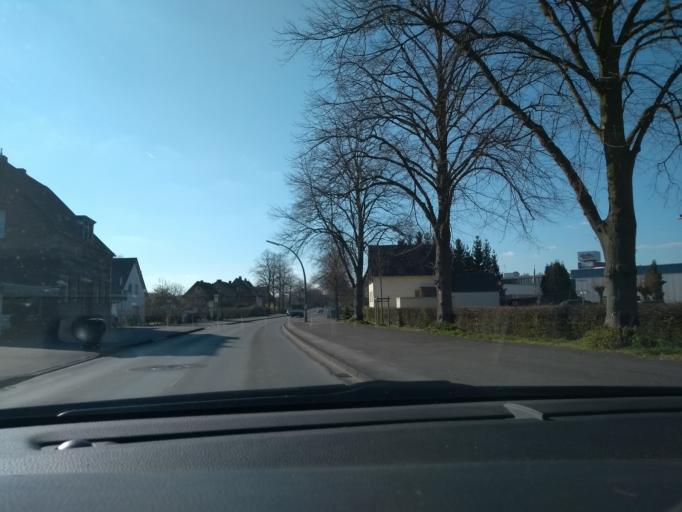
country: DE
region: North Rhine-Westphalia
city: Lunen
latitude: 51.6242
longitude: 7.5050
